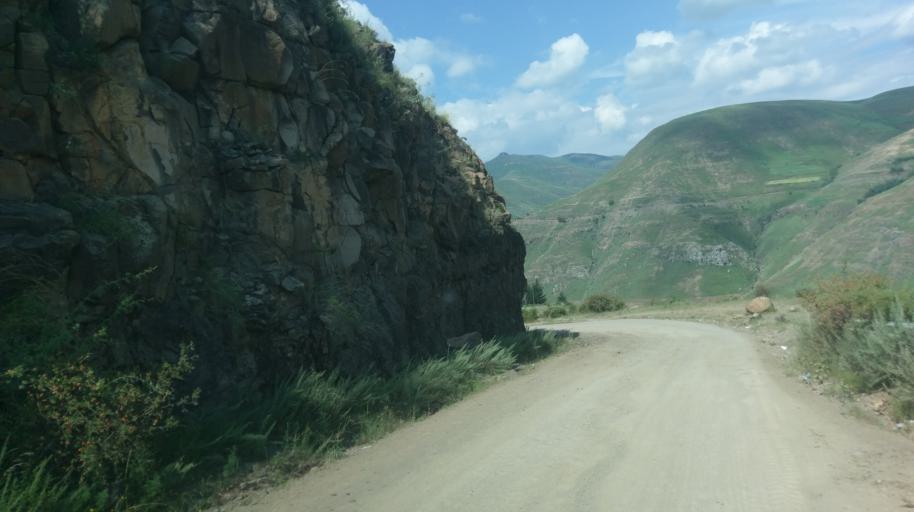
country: LS
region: Butha-Buthe
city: Butha-Buthe
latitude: -29.1052
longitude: 28.4998
